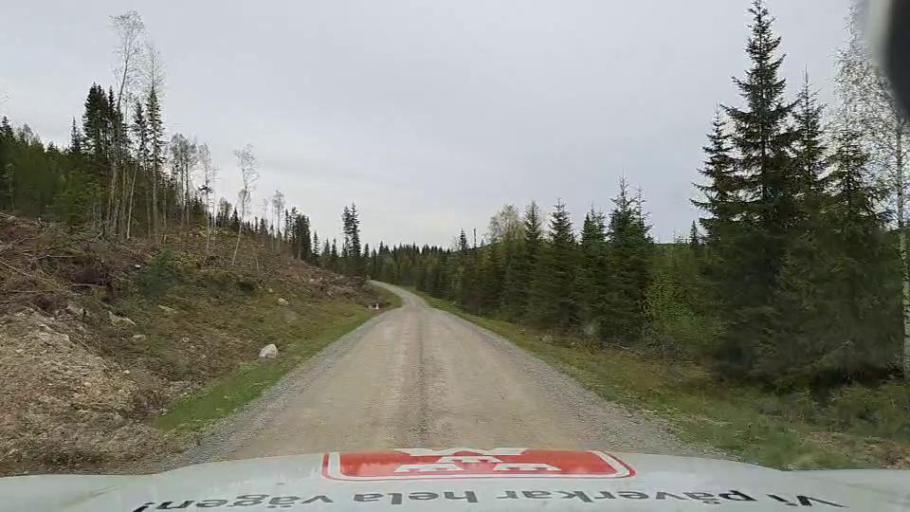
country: SE
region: Jaemtland
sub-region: Bergs Kommun
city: Hoverberg
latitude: 62.5528
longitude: 14.6916
